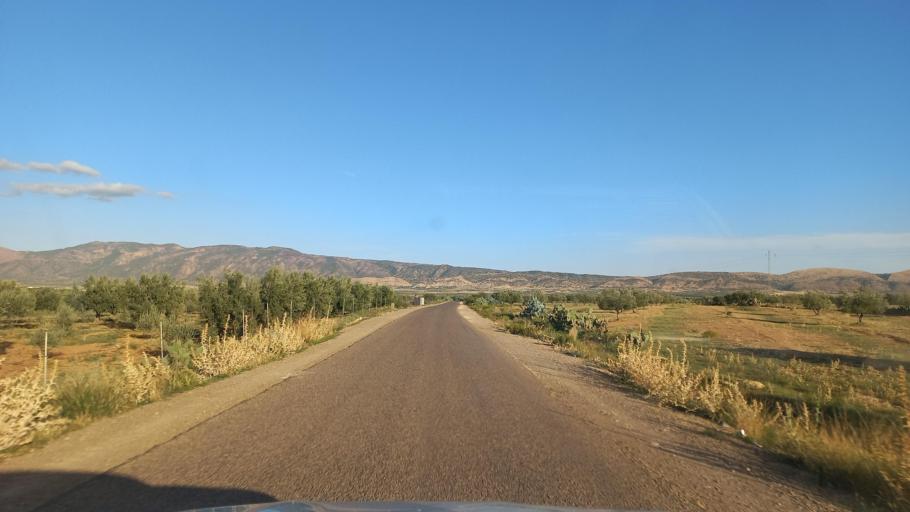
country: TN
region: Al Qasrayn
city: Sbiba
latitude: 35.4129
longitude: 9.1268
